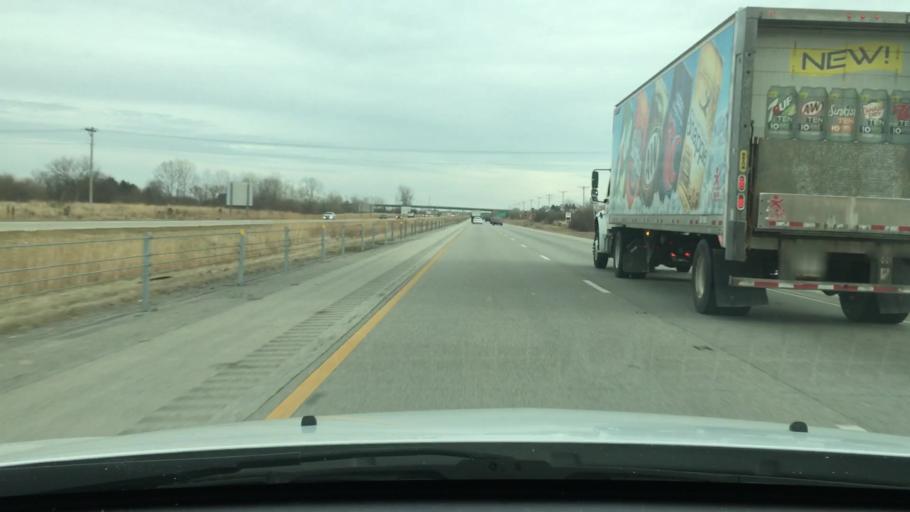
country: US
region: Illinois
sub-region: Sangamon County
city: Jerome
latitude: 39.7418
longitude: -89.6974
